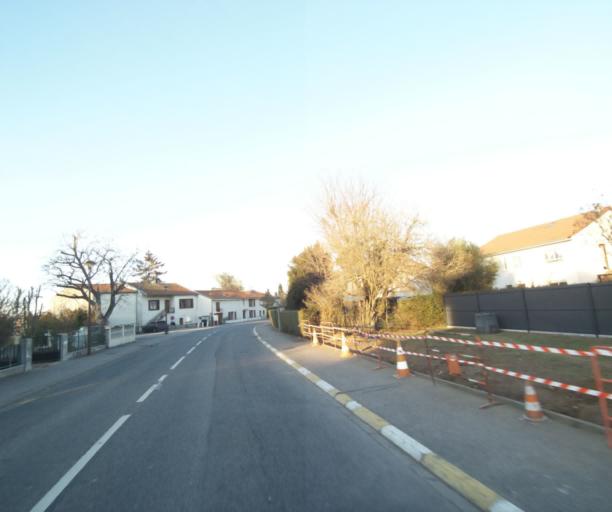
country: FR
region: Lorraine
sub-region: Departement de Meurthe-et-Moselle
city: Pulnoy
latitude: 48.7011
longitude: 6.2569
